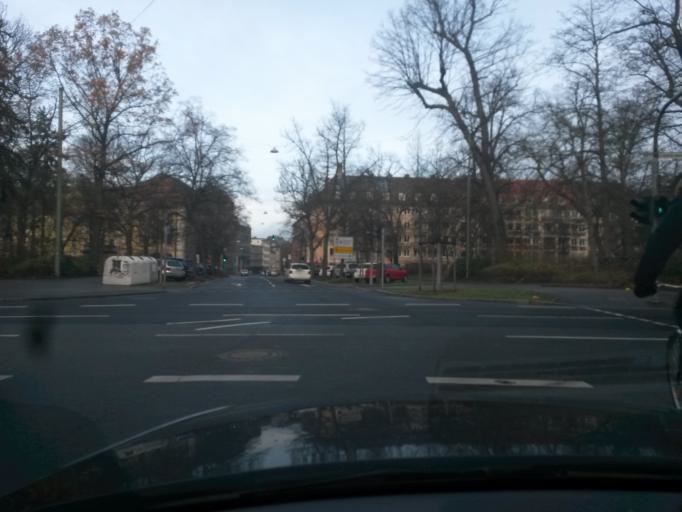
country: DE
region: Bavaria
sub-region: Regierungsbezirk Unterfranken
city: Wuerzburg
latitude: 49.7863
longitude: 9.9346
